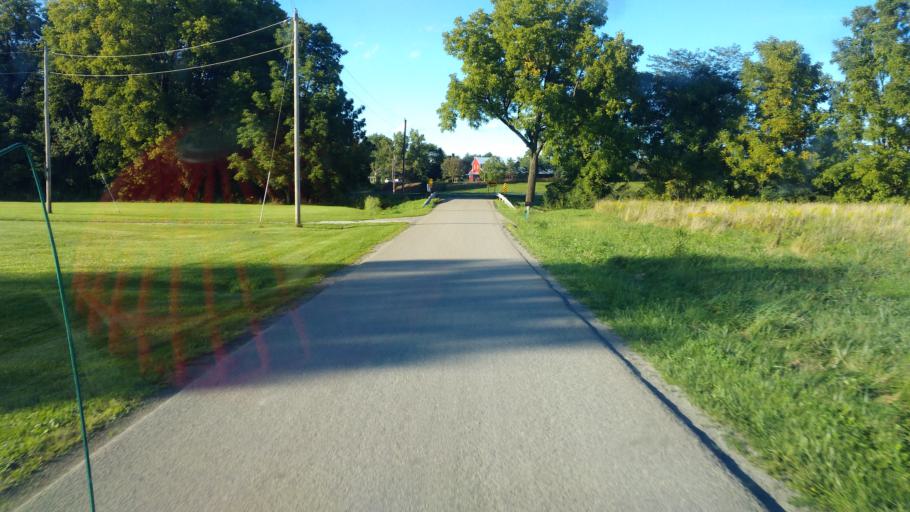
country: US
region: Ohio
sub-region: Wyandot County
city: Upper Sandusky
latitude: 40.8093
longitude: -83.3807
